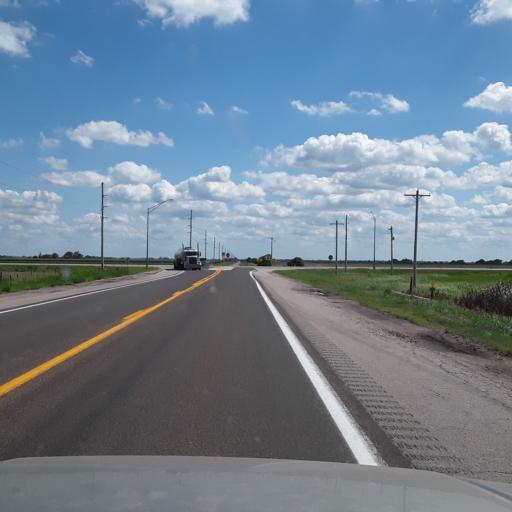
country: US
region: Nebraska
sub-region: Merrick County
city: Central City
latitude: 41.1926
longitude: -97.9829
